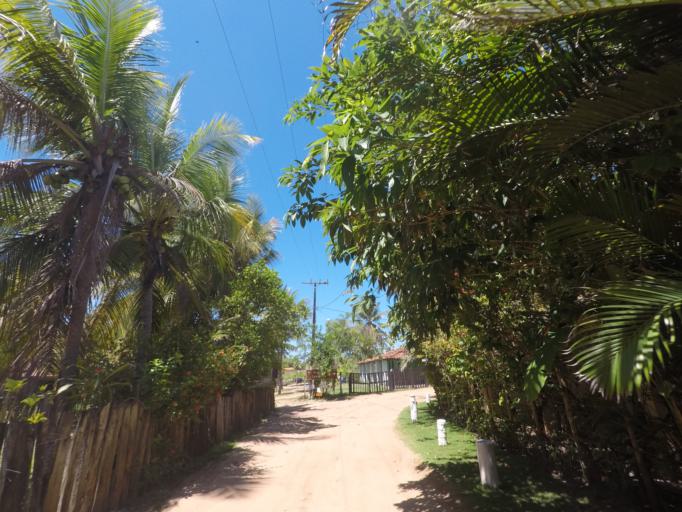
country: BR
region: Bahia
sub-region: Marau
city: Marau
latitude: -14.0213
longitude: -38.9472
